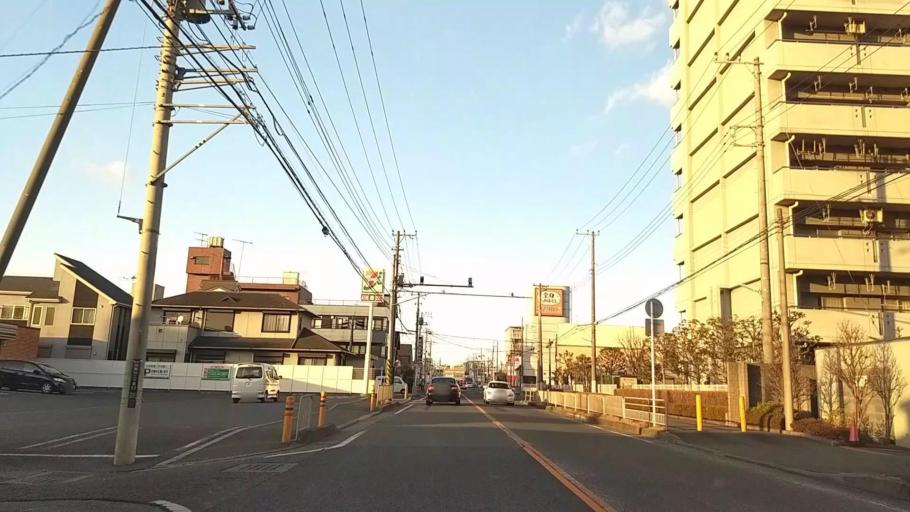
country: JP
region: Kanagawa
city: Atsugi
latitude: 35.4470
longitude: 139.3779
